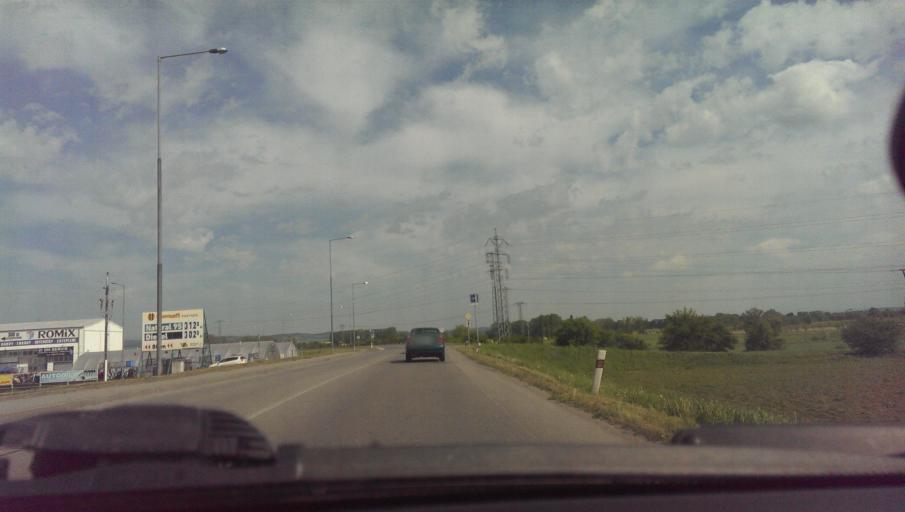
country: CZ
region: Zlin
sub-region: Okres Uherske Hradiste
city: Uherske Hradiste
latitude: 49.0790
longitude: 17.4539
